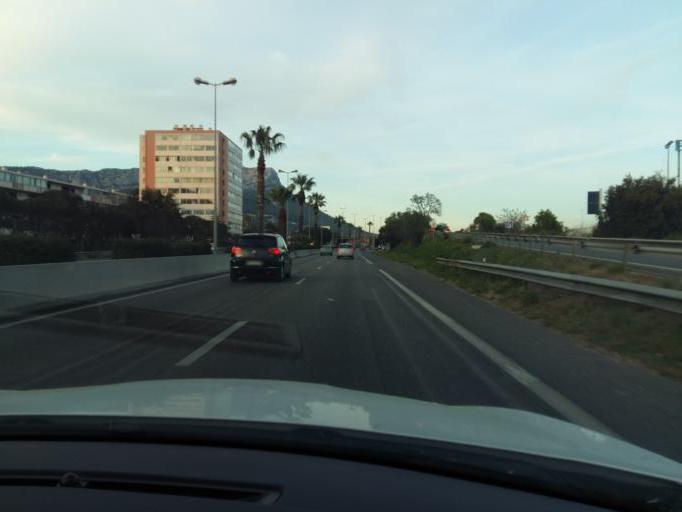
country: FR
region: Provence-Alpes-Cote d'Azur
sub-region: Departement du Var
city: La Valette-du-Var
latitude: 43.1306
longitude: 5.9792
